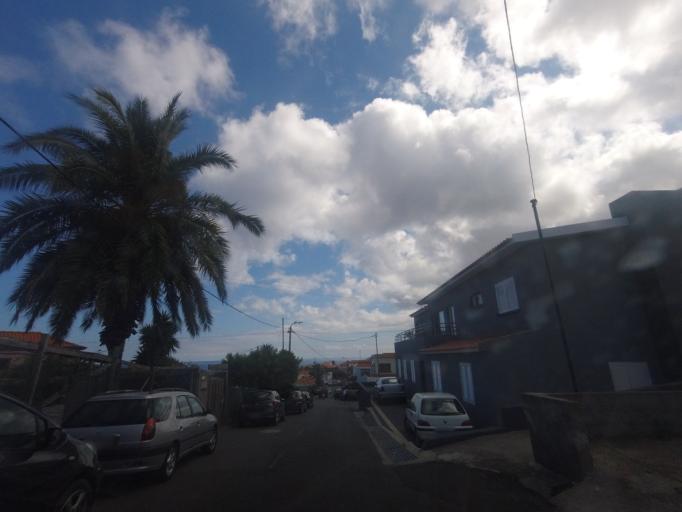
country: PT
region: Madeira
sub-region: Machico
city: Canical
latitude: 32.7412
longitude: -16.7405
